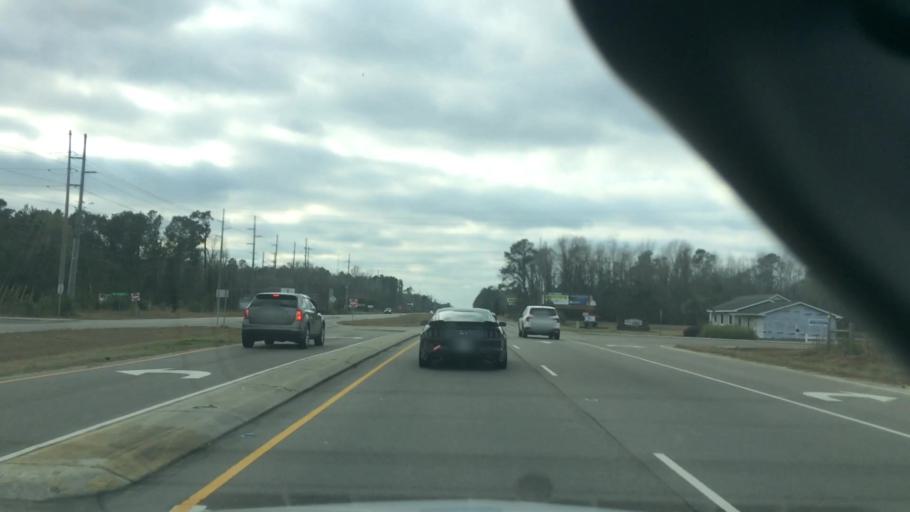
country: US
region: North Carolina
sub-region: Brunswick County
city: Shallotte
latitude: 34.0074
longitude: -78.3012
